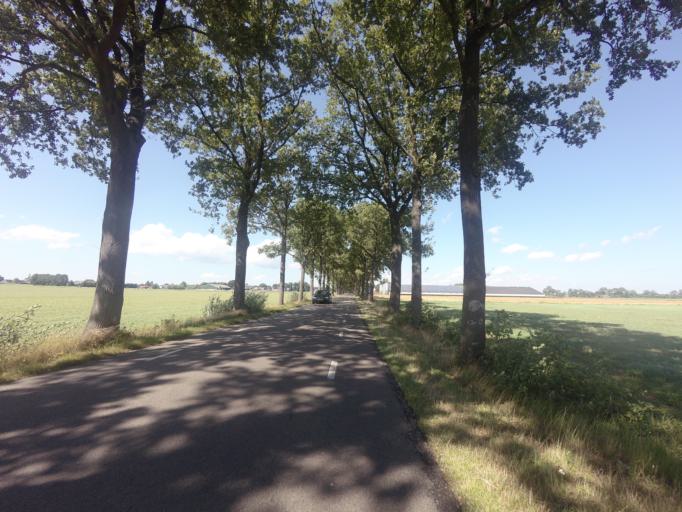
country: NL
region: Overijssel
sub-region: Gemeente Twenterand
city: Den Ham
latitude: 52.5575
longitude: 6.4353
